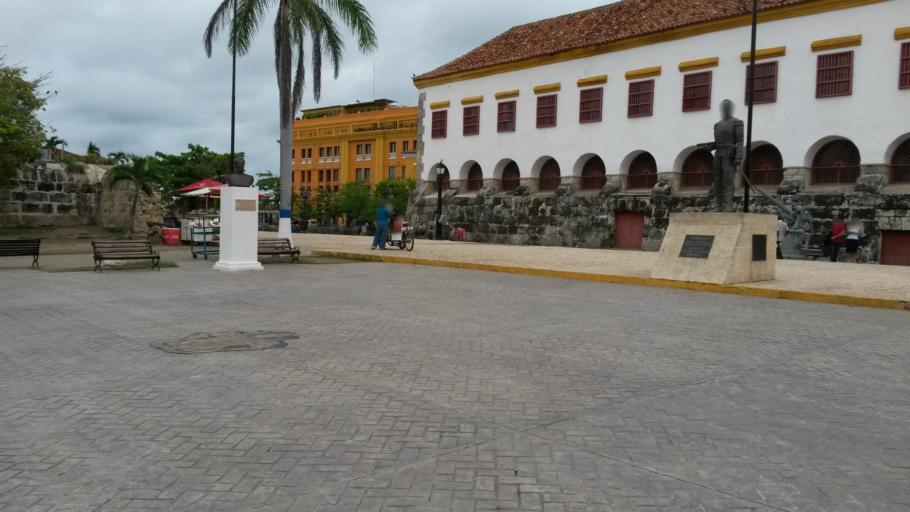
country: CO
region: Bolivar
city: Cartagena
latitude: 10.4213
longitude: -75.5519
